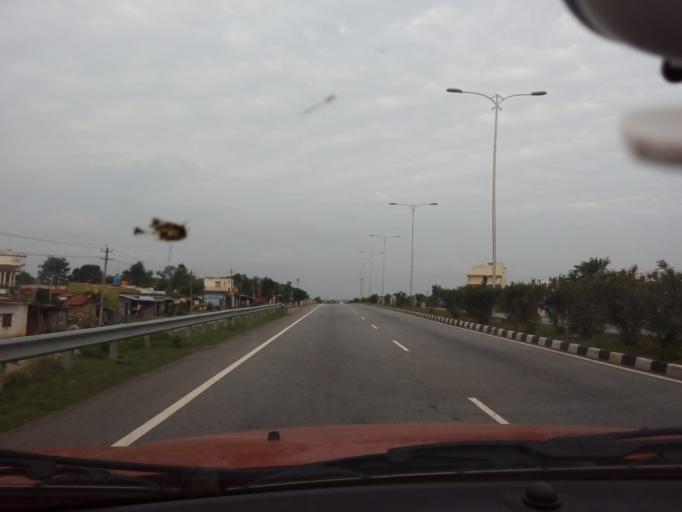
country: IN
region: Karnataka
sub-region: Mandya
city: Belluru
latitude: 12.9811
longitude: 76.8605
